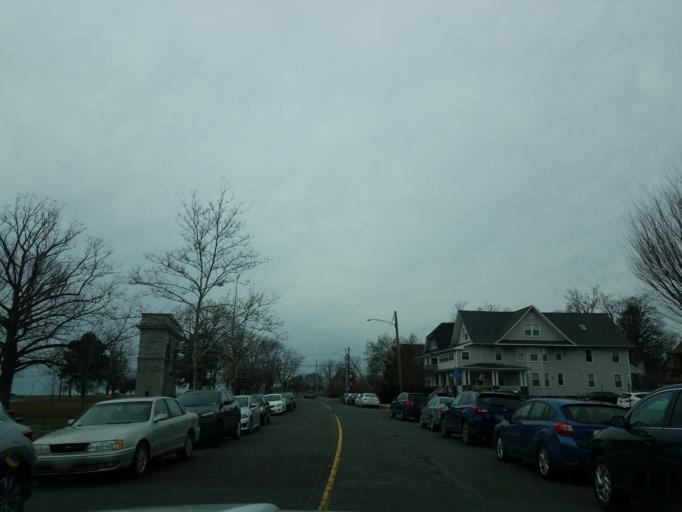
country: US
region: Connecticut
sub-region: Fairfield County
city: Bridgeport
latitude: 41.1635
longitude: -73.1882
